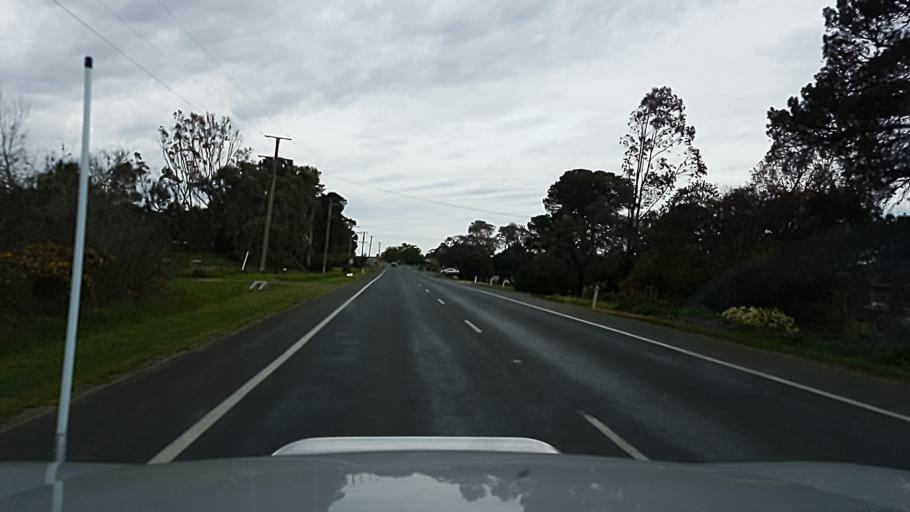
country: AU
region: Victoria
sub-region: Ballarat North
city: Mount Clear
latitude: -37.7791
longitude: 144.0290
